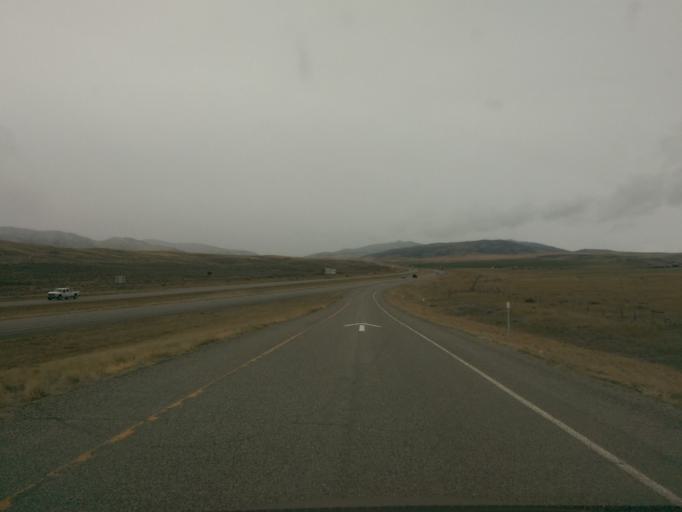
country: US
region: Montana
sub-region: Gallatin County
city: Three Forks
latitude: 45.9154
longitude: -111.7444
